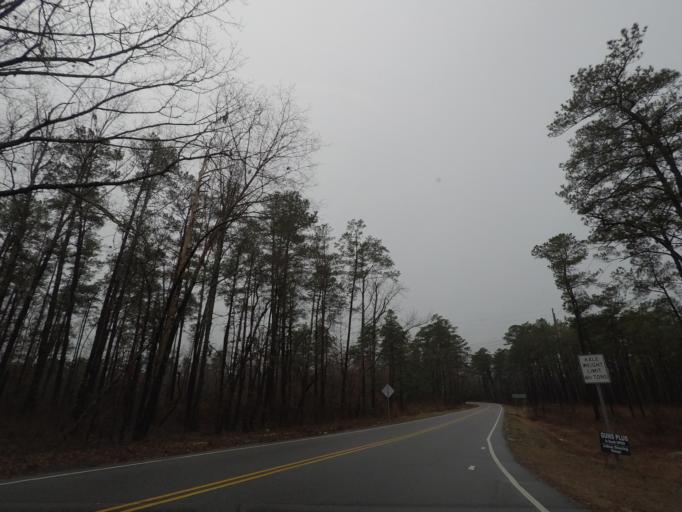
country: US
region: North Carolina
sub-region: Cumberland County
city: Spring Lake
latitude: 35.2571
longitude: -78.9913
